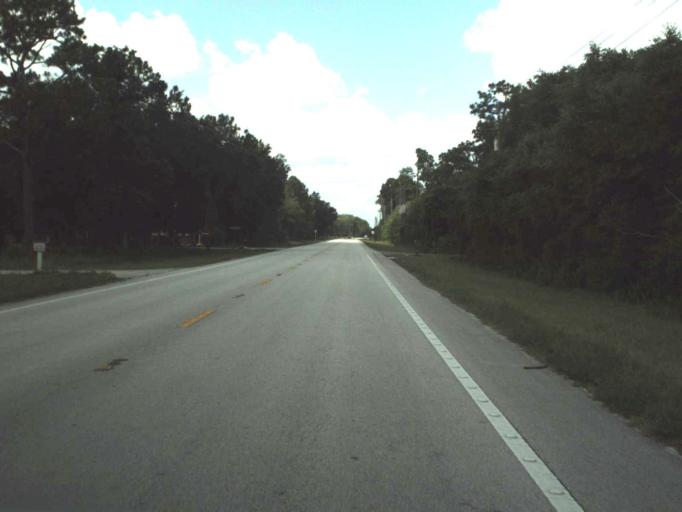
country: US
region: Florida
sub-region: Volusia County
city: Lake Helen
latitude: 28.9280
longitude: -81.1130
